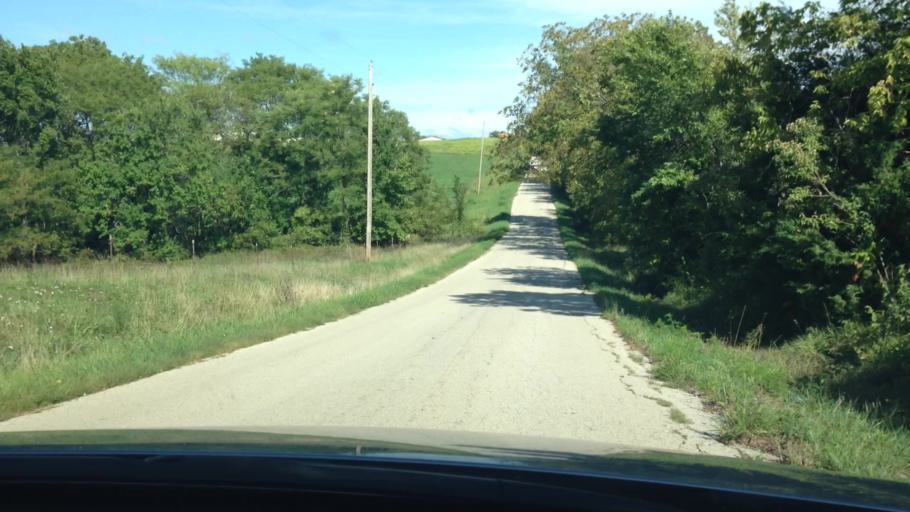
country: US
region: Missouri
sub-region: Clay County
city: Smithville
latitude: 39.3401
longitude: -94.6662
